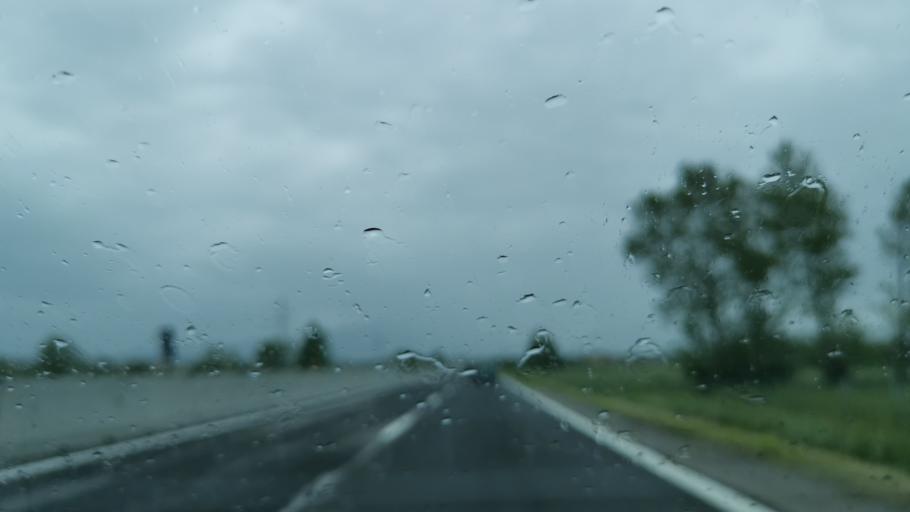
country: IT
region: Veneto
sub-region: Provincia di Verona
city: Castelnuovo del Garda
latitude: 45.4483
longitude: 10.7479
